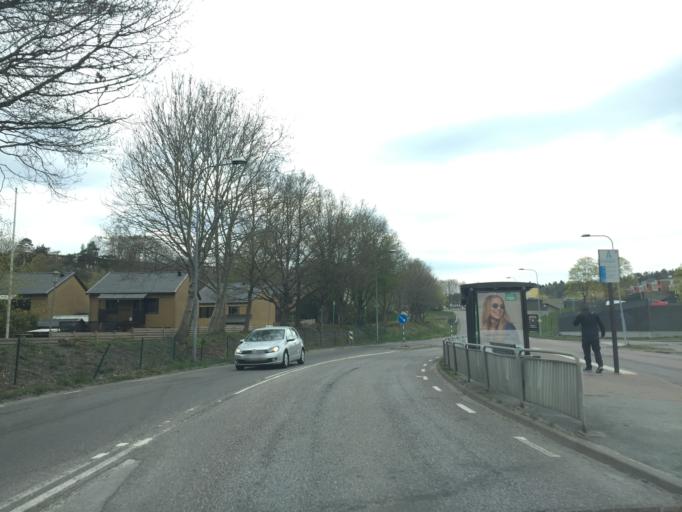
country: SE
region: Vaestra Goetaland
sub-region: Goteborg
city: Loevgaerdet
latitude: 57.8123
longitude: 12.0397
